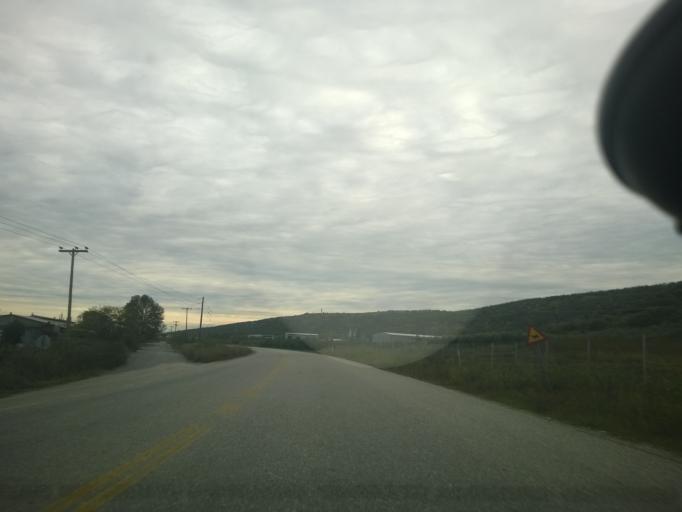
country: GR
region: Central Macedonia
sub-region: Nomos Pellis
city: Profitis Ilias
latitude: 40.8072
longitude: 22.1463
